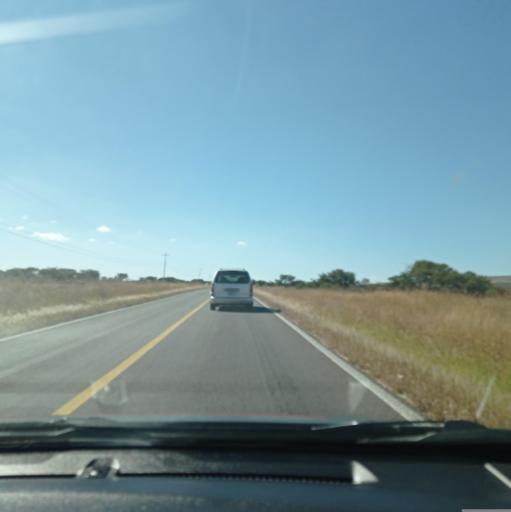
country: MX
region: Jalisco
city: San Miguel el Alto
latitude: 21.0203
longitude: -102.4534
